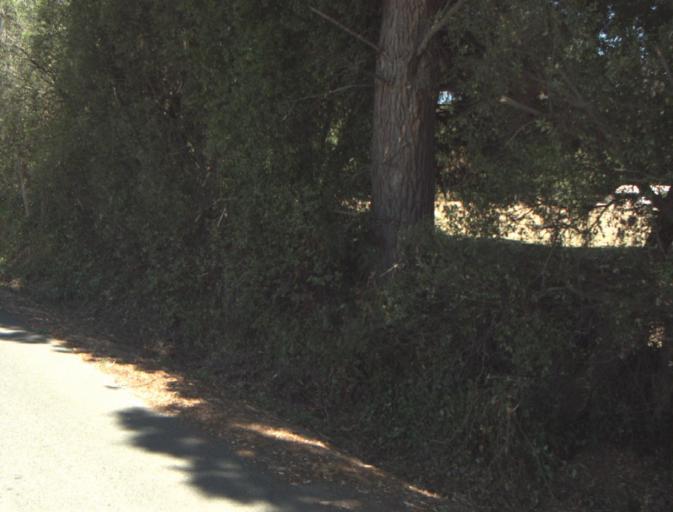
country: AU
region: Tasmania
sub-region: Launceston
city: Mayfield
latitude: -41.2606
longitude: 147.1357
